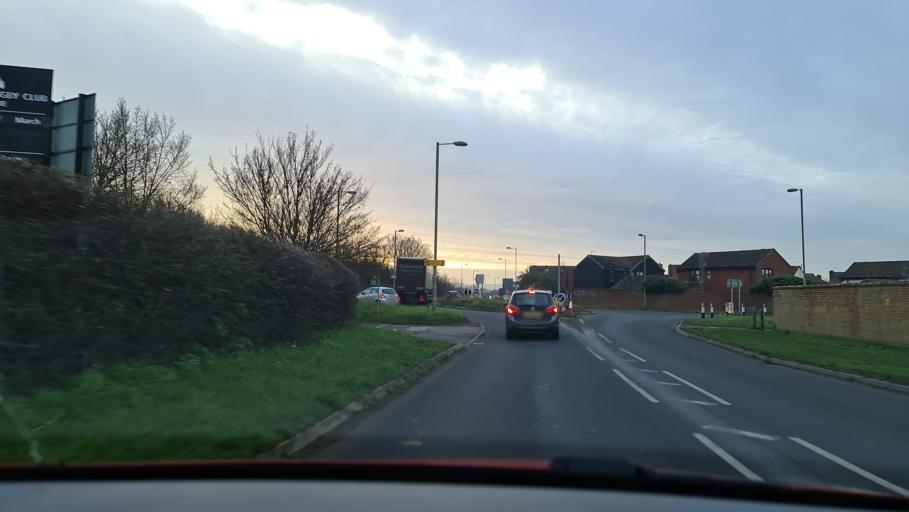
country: GB
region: England
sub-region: Oxfordshire
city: Thame
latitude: 51.7476
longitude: -0.9597
